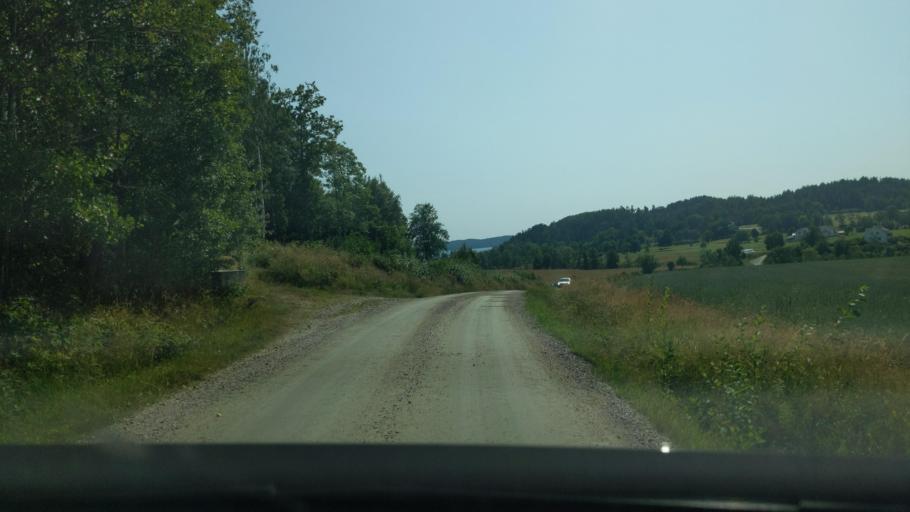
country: SE
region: Vaestra Goetaland
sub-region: Uddevalla Kommun
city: Uddevalla
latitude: 58.3393
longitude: 11.8104
